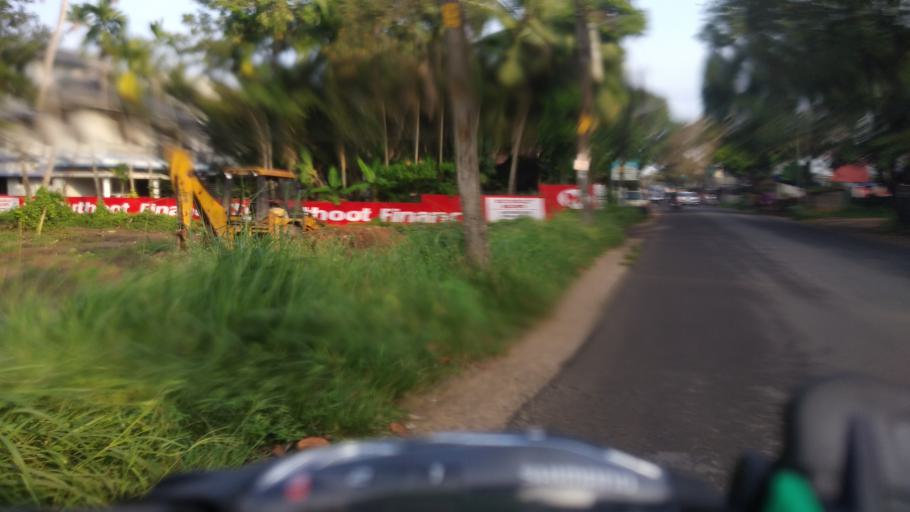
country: IN
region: Kerala
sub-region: Ernakulam
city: Elur
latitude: 10.0772
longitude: 76.2109
